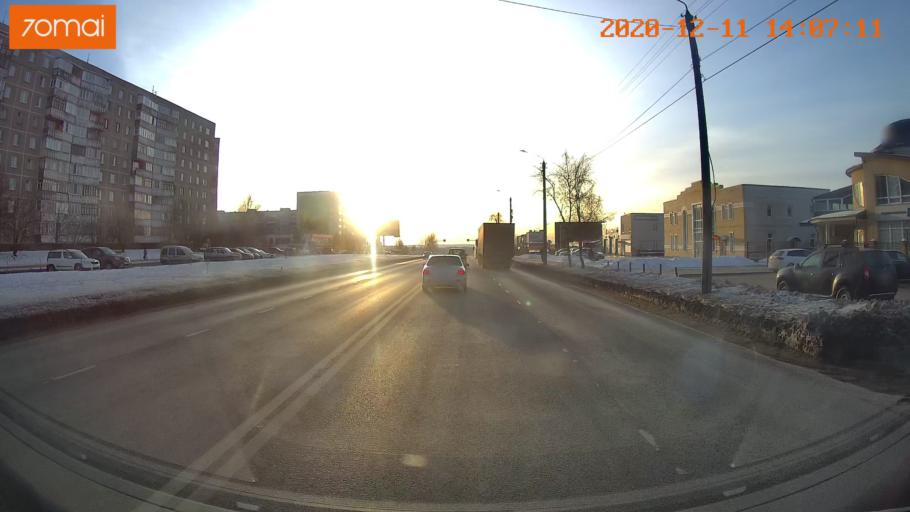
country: RU
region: Kostroma
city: Oktyabr'skiy
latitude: 57.7392
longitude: 41.0006
